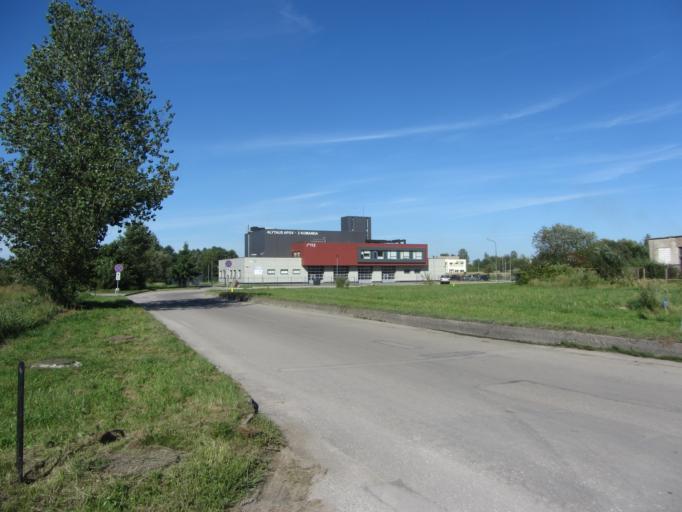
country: LT
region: Alytaus apskritis
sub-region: Alytus
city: Alytus
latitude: 54.4399
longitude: 24.0070
